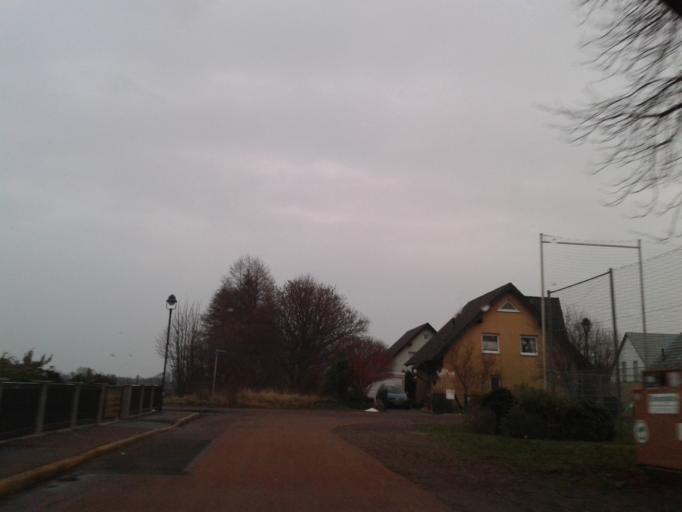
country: DE
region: Saxony-Anhalt
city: Peissen
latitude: 51.4942
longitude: 12.0334
